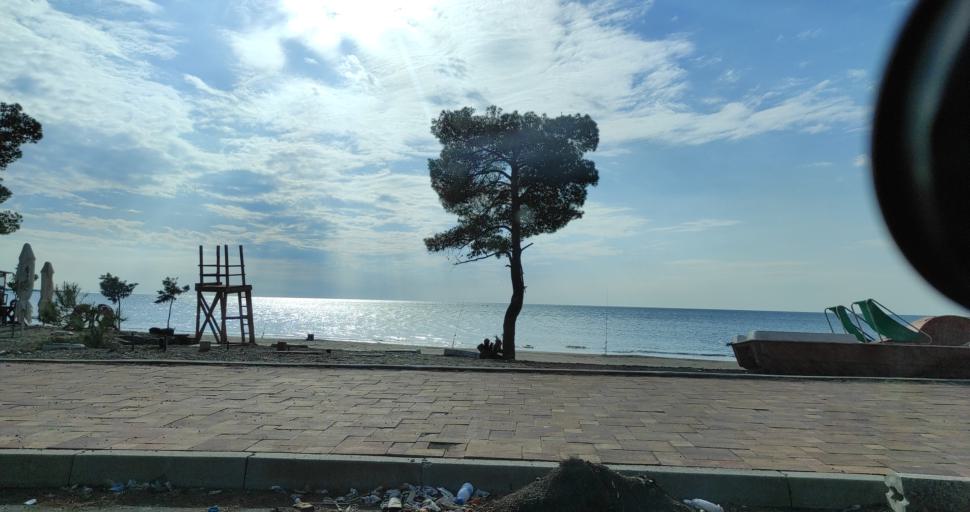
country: AL
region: Lezhe
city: Shengjin
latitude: 41.7946
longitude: 19.6022
